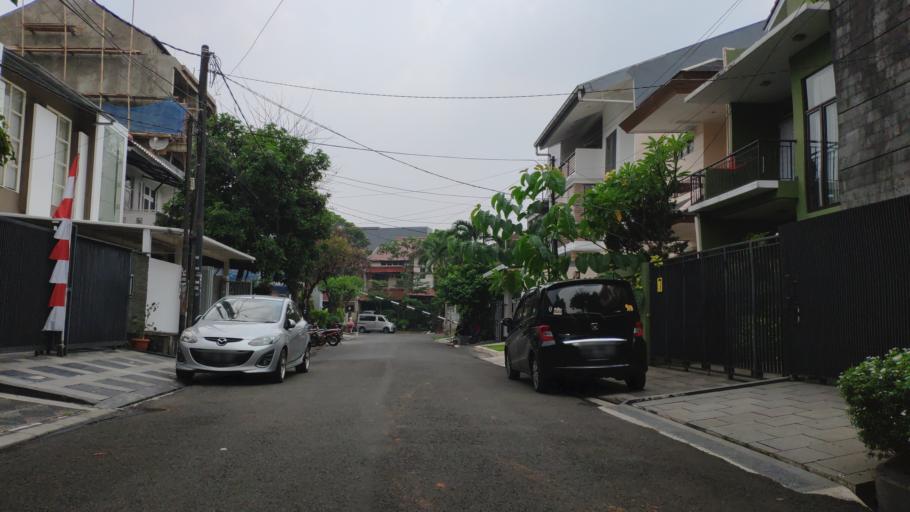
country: ID
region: Banten
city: South Tangerang
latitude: -6.2672
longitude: 106.7778
